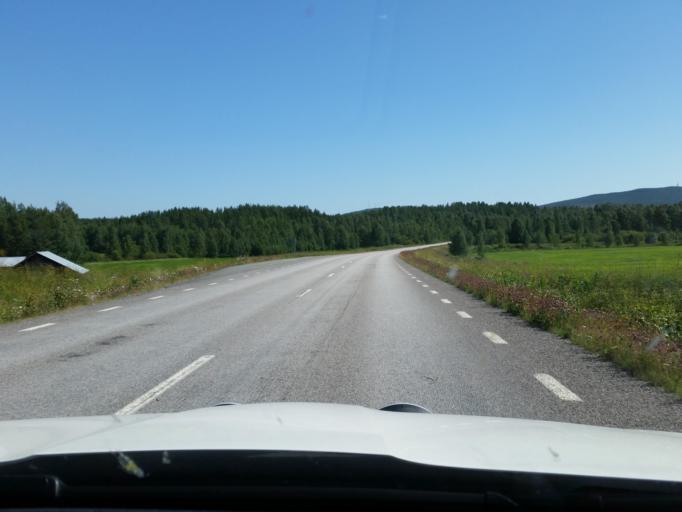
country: SE
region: Norrbotten
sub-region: Alvsbyns Kommun
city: AElvsbyn
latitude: 65.6738
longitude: 20.8465
